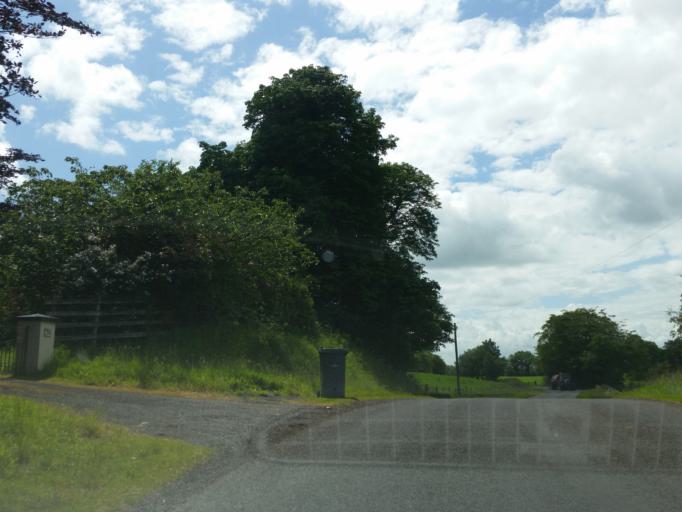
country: GB
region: Northern Ireland
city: Fivemiletown
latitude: 54.3683
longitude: -7.3096
